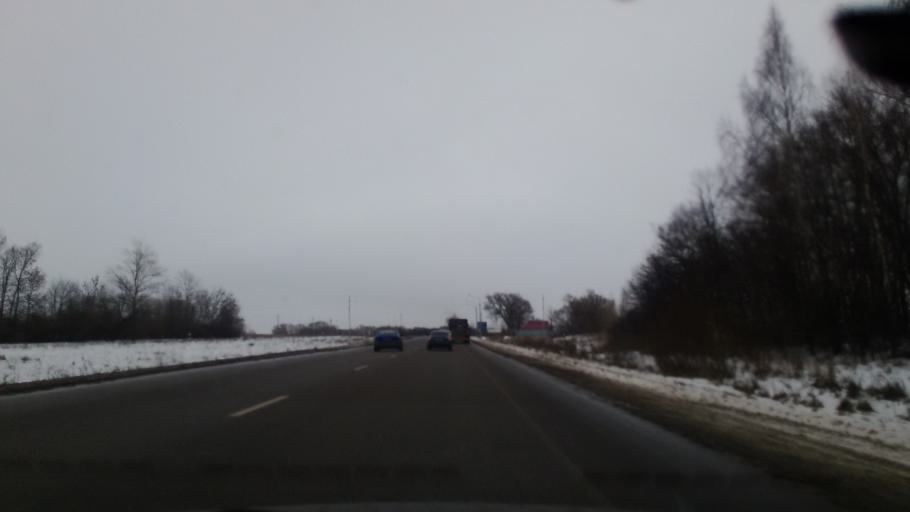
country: RU
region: Tula
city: Borodinskiy
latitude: 54.0292
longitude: 37.8853
